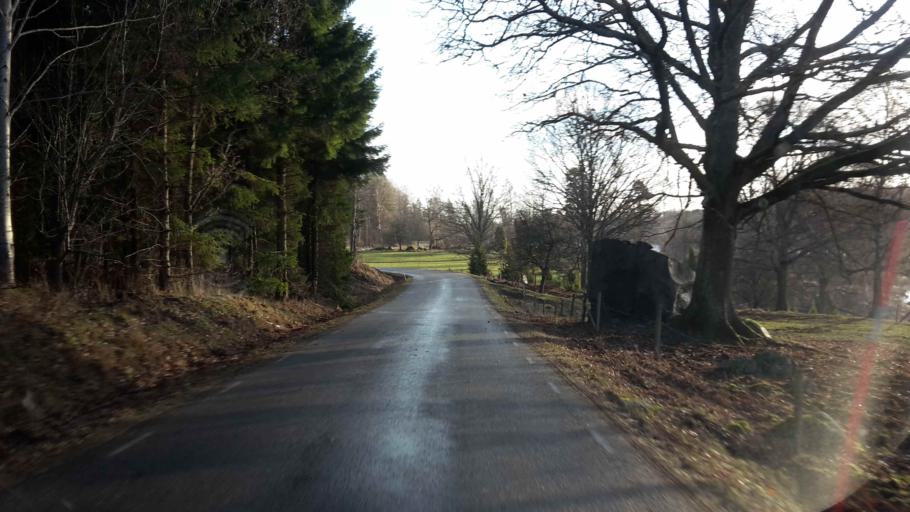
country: SE
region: OEstergoetland
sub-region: Atvidabergs Kommun
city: Atvidaberg
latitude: 58.2804
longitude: 16.0992
